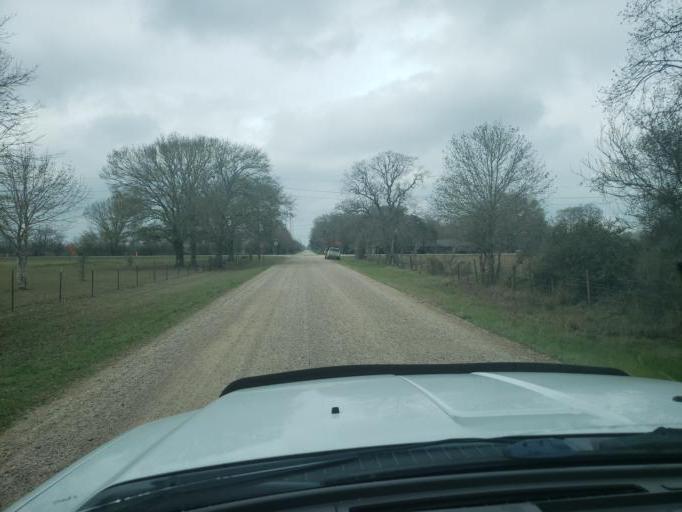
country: US
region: Texas
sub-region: Fort Bend County
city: Needville
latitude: 29.3592
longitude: -95.7654
